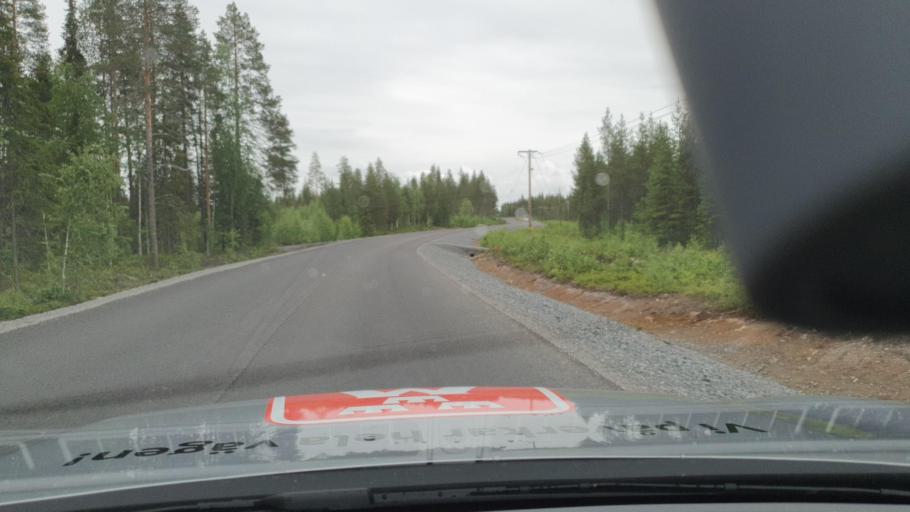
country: SE
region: Norrbotten
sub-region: Overtornea Kommun
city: OEvertornea
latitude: 66.6419
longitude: 23.2505
